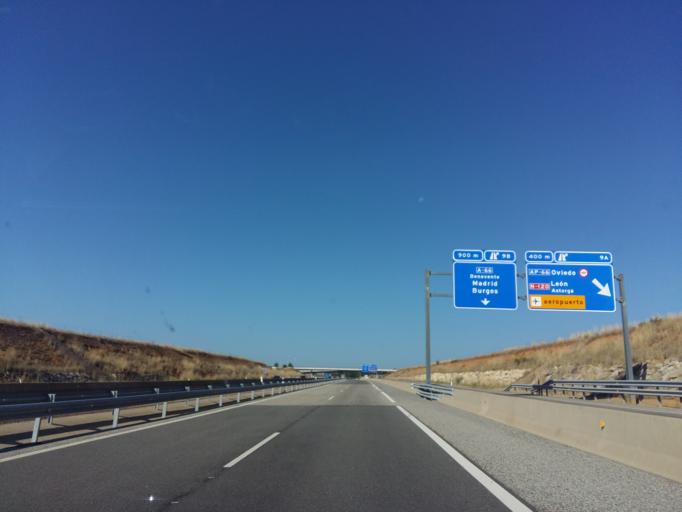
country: ES
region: Castille and Leon
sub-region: Provincia de Leon
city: Valverde de la Virgen
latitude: 42.5703
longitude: -5.6446
